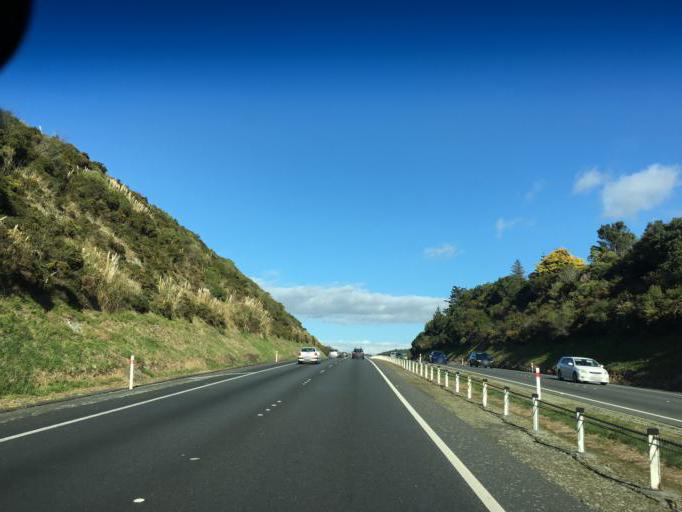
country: NZ
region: Wellington
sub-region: Porirua City
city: Porirua
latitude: -41.1706
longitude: 174.8315
